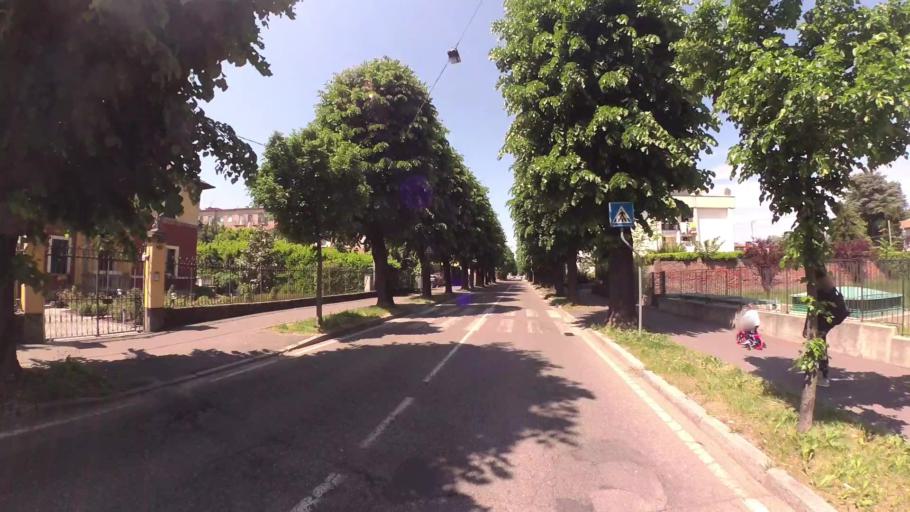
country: IT
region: Lombardy
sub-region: Provincia di Varese
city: Tradate
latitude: 45.7082
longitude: 8.9111
